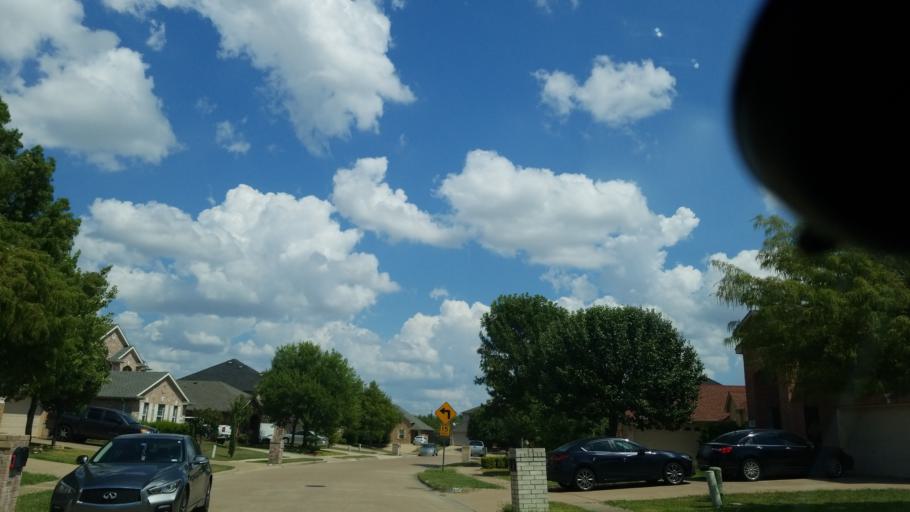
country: US
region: Texas
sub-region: Dallas County
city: Grand Prairie
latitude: 32.7267
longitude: -96.9974
